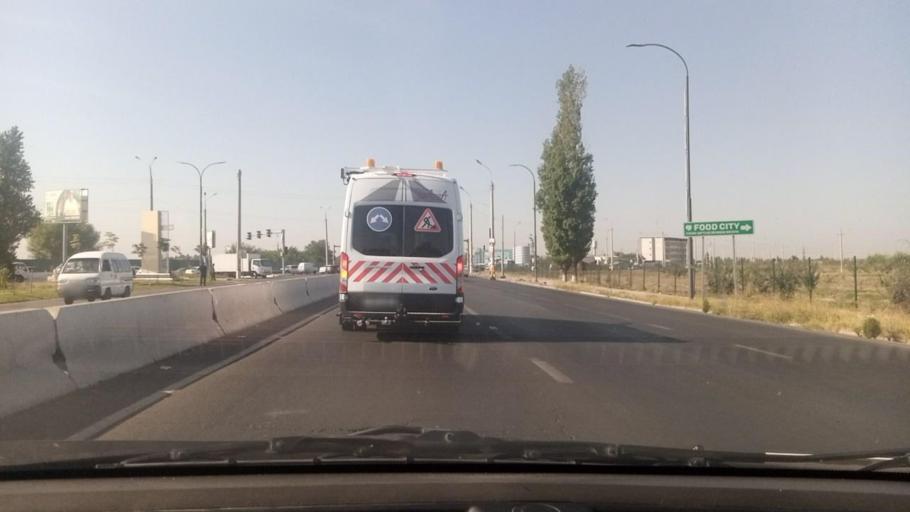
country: UZ
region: Toshkent Shahri
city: Bektemir
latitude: 41.2034
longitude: 69.3326
